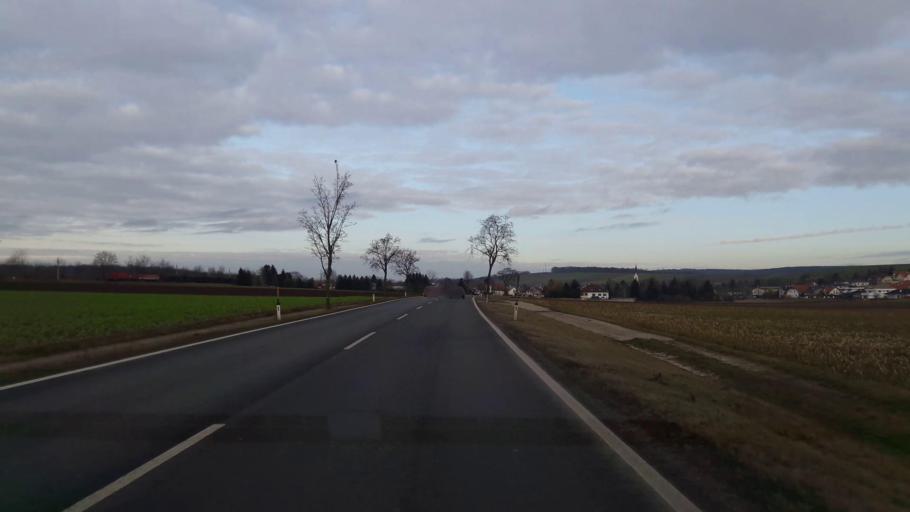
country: AT
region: Lower Austria
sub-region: Politischer Bezirk Mistelbach
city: Mistelbach
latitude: 48.5994
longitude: 16.5430
